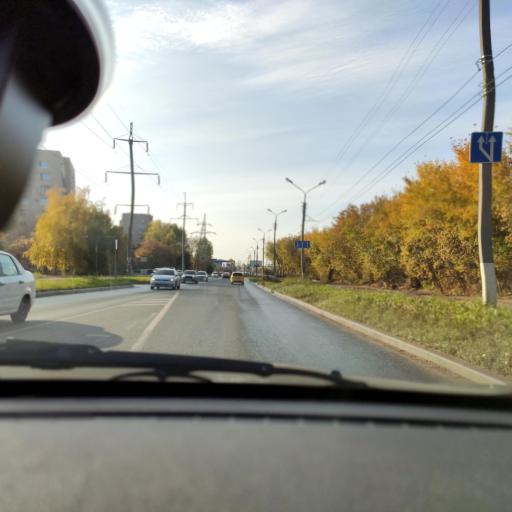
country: RU
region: Samara
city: Tol'yatti
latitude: 53.5274
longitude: 49.3963
